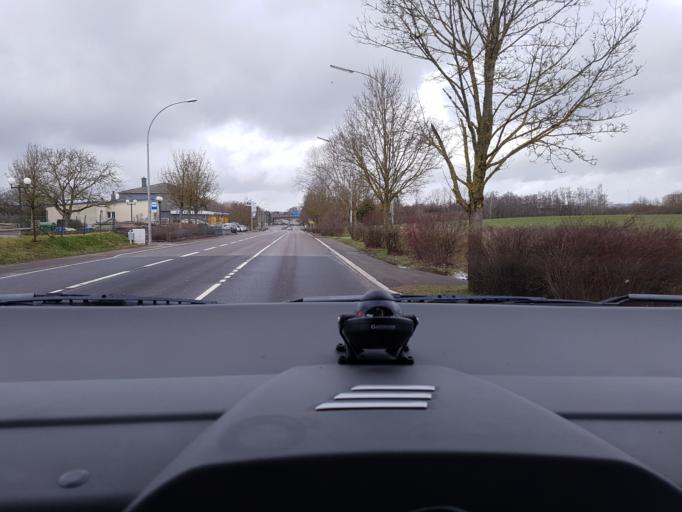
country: LU
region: Luxembourg
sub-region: Canton de Capellen
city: Mamer
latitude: 49.6359
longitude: 6.0133
